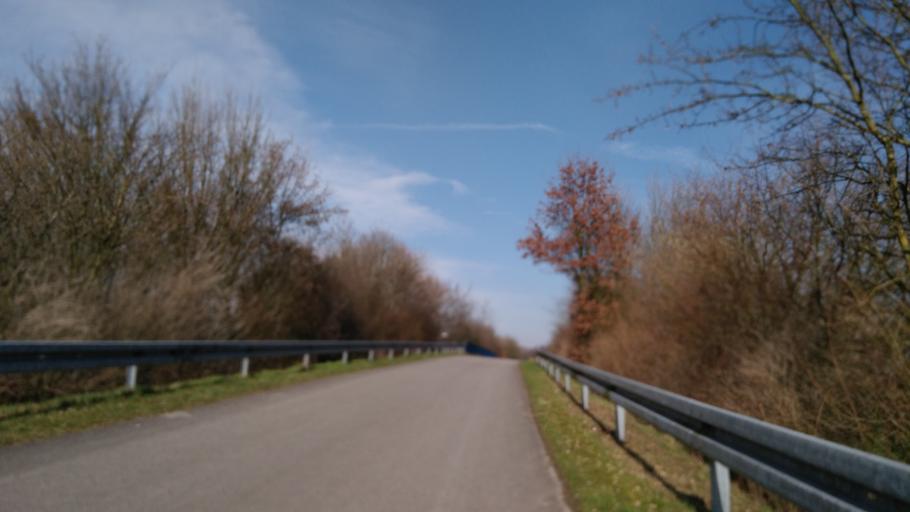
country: DE
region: North Rhine-Westphalia
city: Dorsten
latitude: 51.6777
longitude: 7.0261
